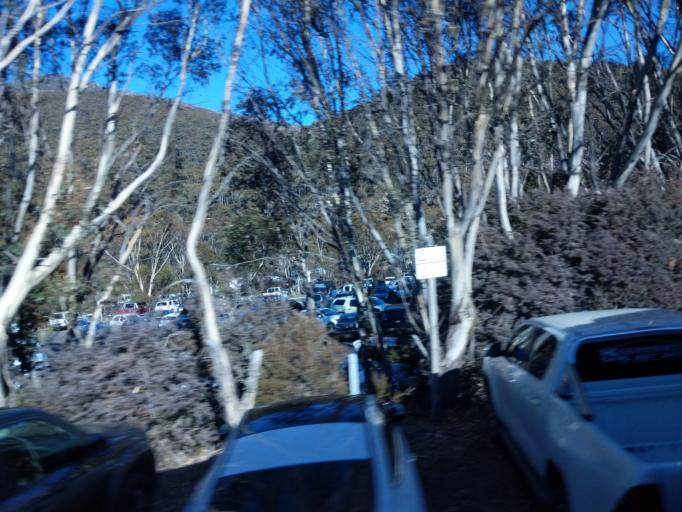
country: AU
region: New South Wales
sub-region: Snowy River
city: Jindabyne
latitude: -36.4980
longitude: 148.3136
